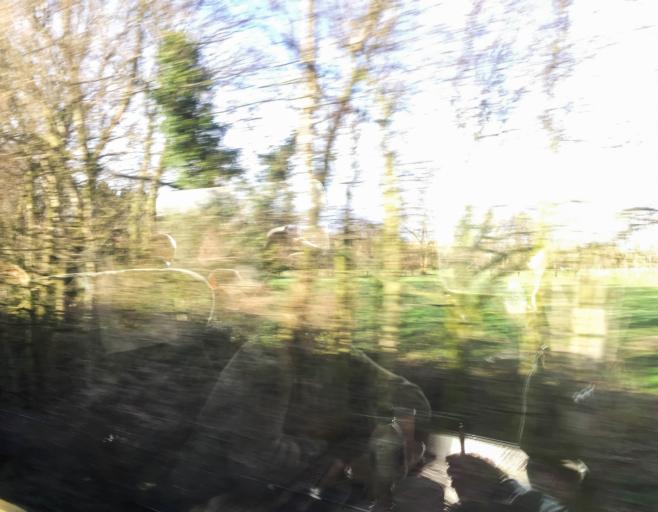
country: GB
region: England
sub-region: Cumbria
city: Carlisle
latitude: 54.9020
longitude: -2.9514
